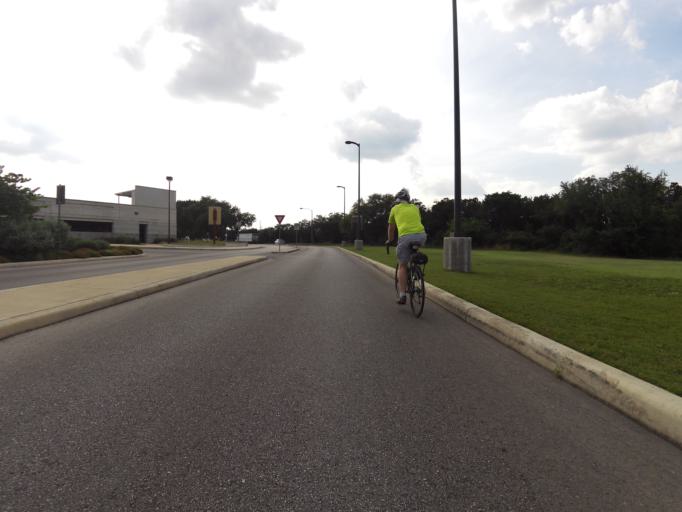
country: US
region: Texas
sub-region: Bexar County
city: Shavano Park
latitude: 29.5873
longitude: -98.6200
